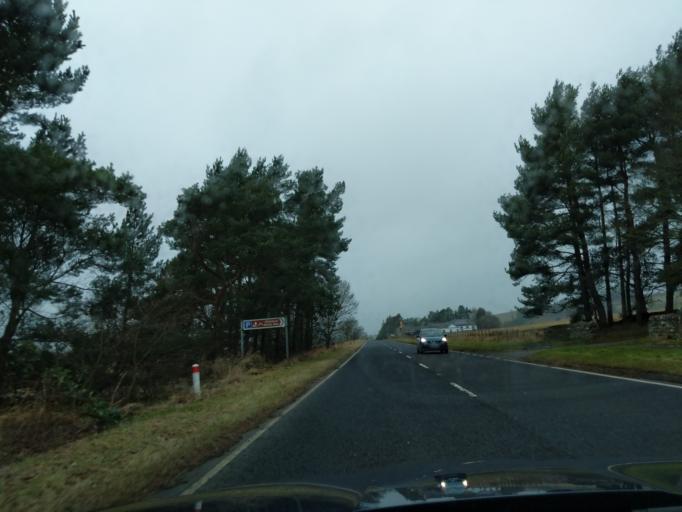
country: GB
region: England
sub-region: Northumberland
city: Otterburn
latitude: 55.2360
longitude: -2.1951
